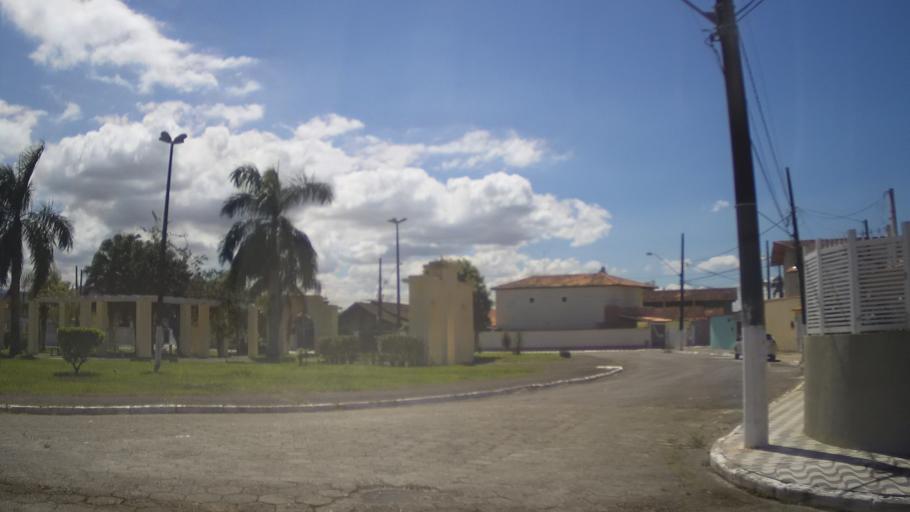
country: BR
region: Sao Paulo
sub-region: Mongagua
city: Mongagua
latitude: -24.0464
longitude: -46.5213
